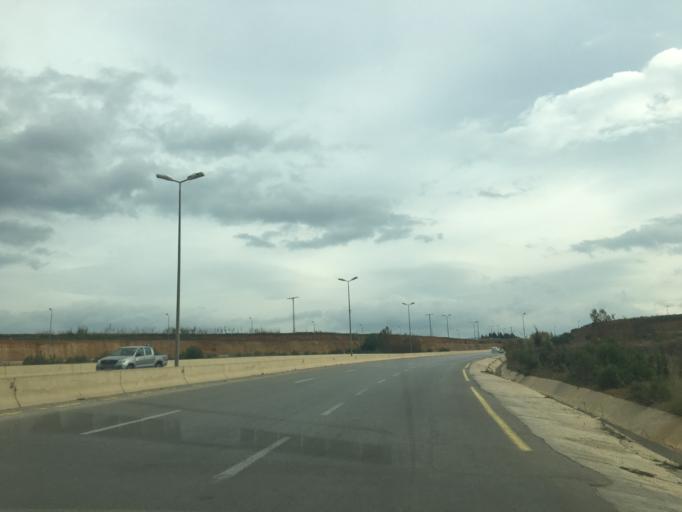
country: DZ
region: Tipaza
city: Tipasa
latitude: 36.5768
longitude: 2.4252
